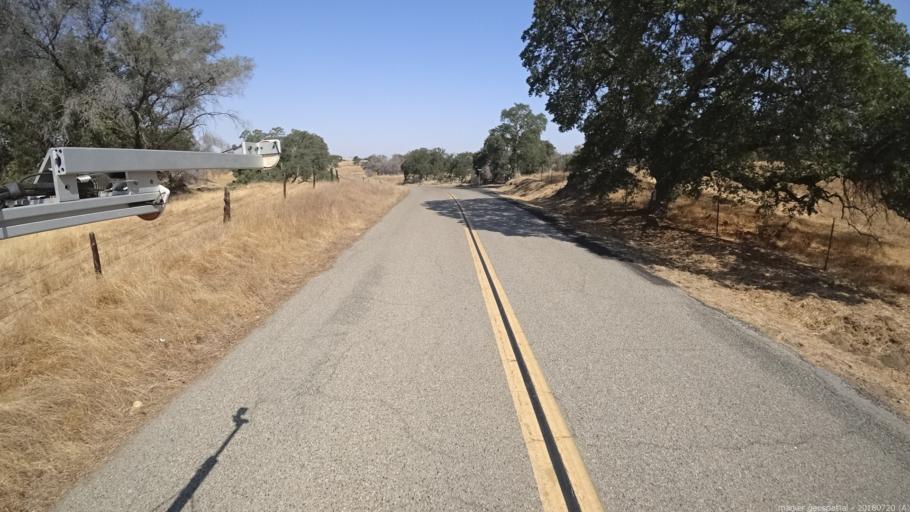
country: US
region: California
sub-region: Madera County
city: Yosemite Lakes
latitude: 37.2327
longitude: -119.9168
